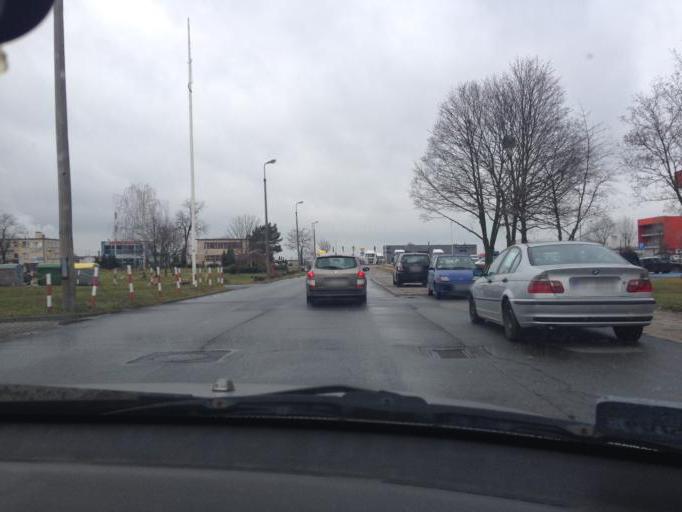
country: PL
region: Opole Voivodeship
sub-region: Powiat opolski
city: Opole
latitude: 50.6829
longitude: 17.9441
